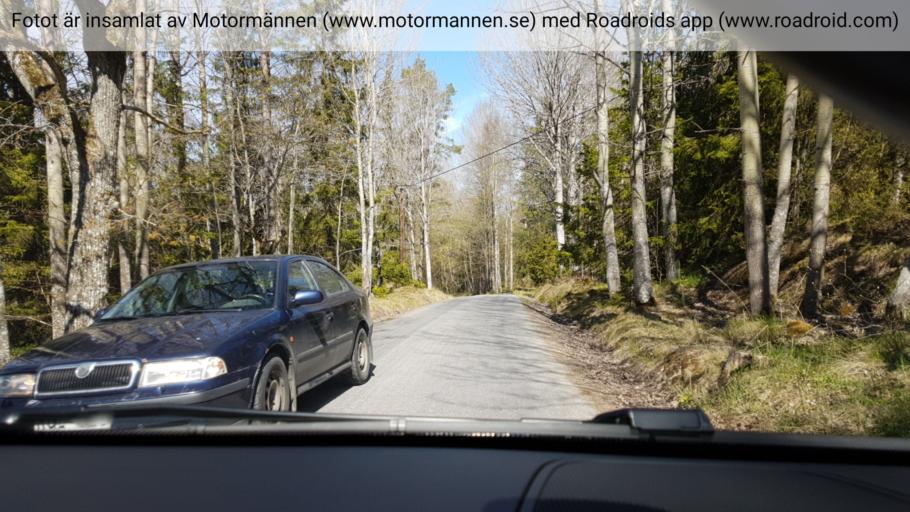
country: SE
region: Stockholm
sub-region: Haninge Kommun
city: Jordbro
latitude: 59.0099
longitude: 18.1186
